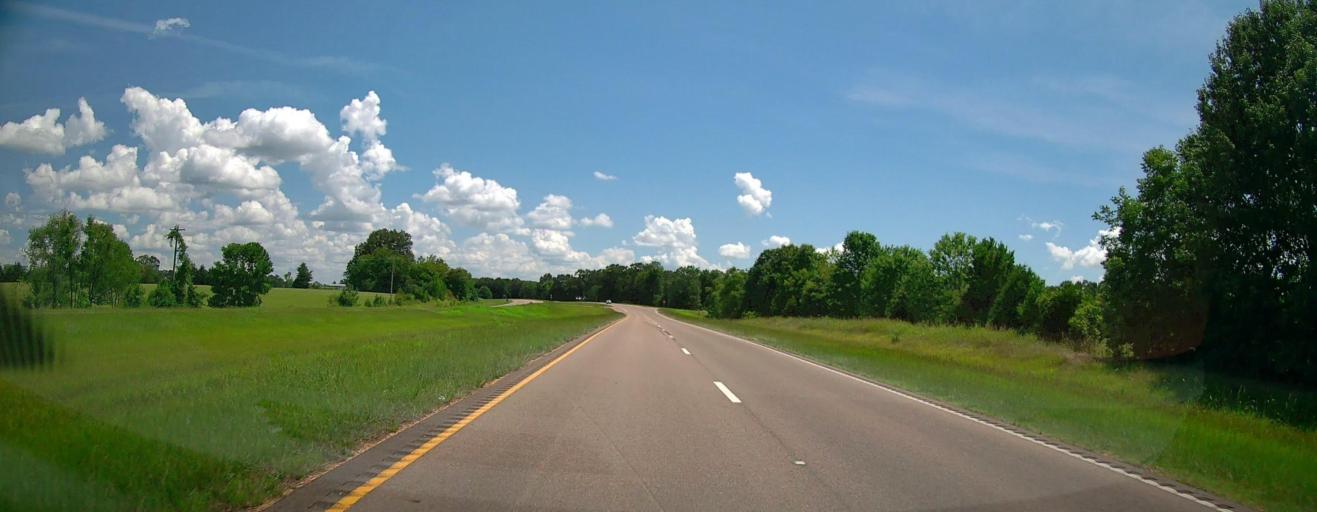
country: US
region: Mississippi
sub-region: Lee County
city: Nettleton
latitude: 33.9674
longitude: -88.6139
